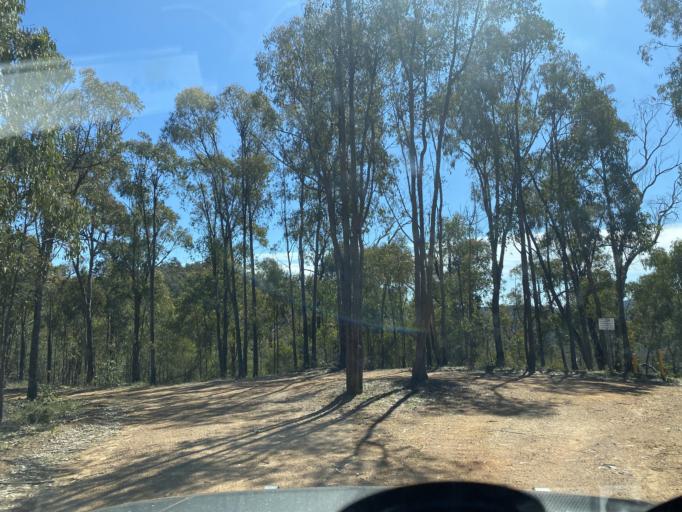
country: AU
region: Victoria
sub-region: Benalla
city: Benalla
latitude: -36.7313
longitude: 146.1831
